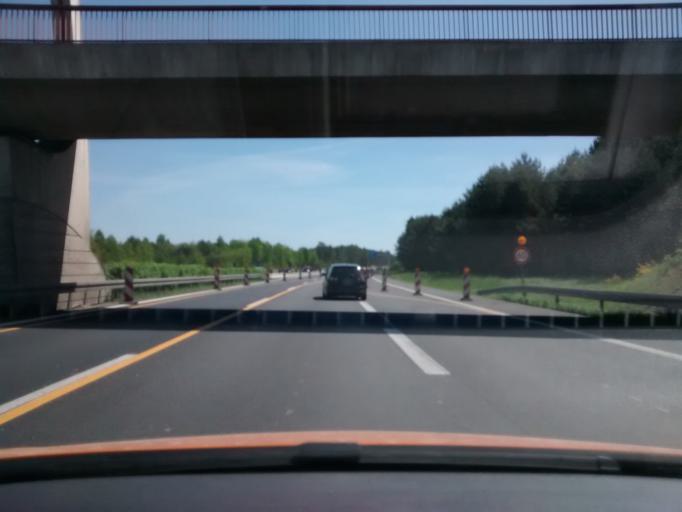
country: DE
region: Brandenburg
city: Erkner
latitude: 52.3233
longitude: 13.7601
